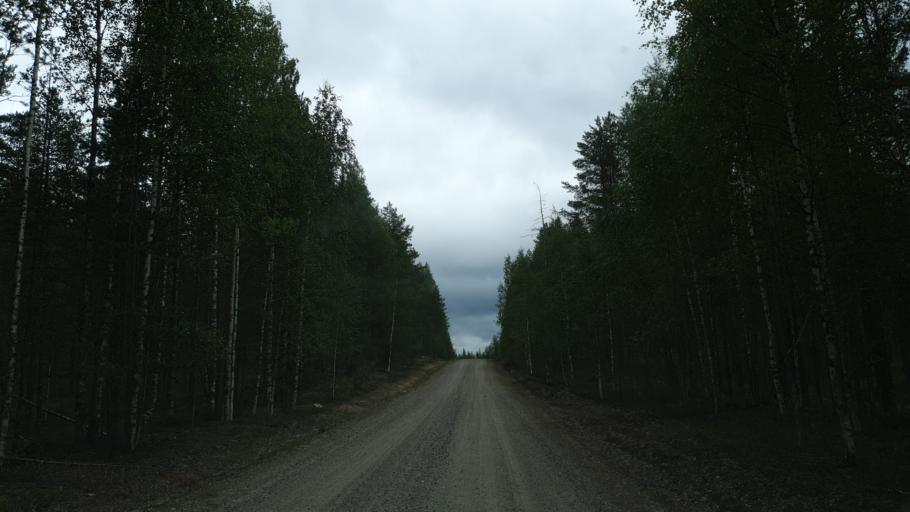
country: FI
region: Kainuu
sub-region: Kehys-Kainuu
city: Kuhmo
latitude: 64.2096
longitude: 29.1672
